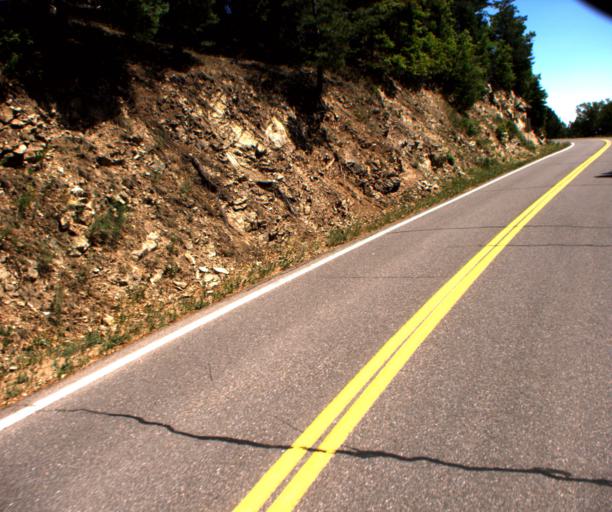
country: US
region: Arizona
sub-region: Graham County
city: Swift Trail Junction
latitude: 32.6455
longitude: -109.8563
